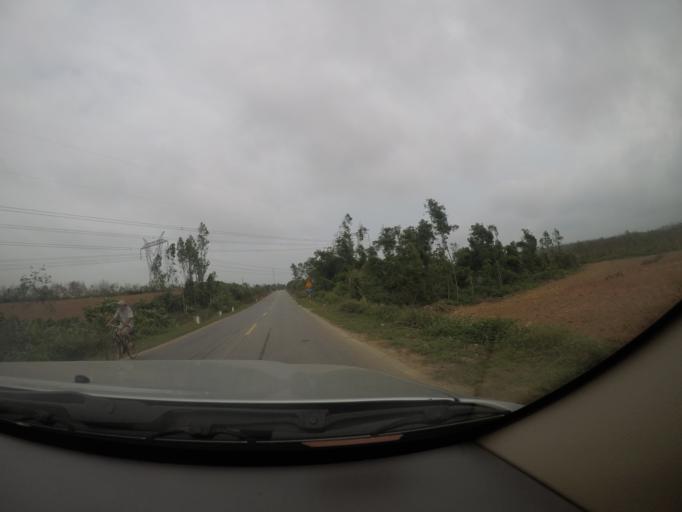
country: VN
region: Quang Binh
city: Hoan Lao
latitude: 17.4907
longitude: 106.5197
